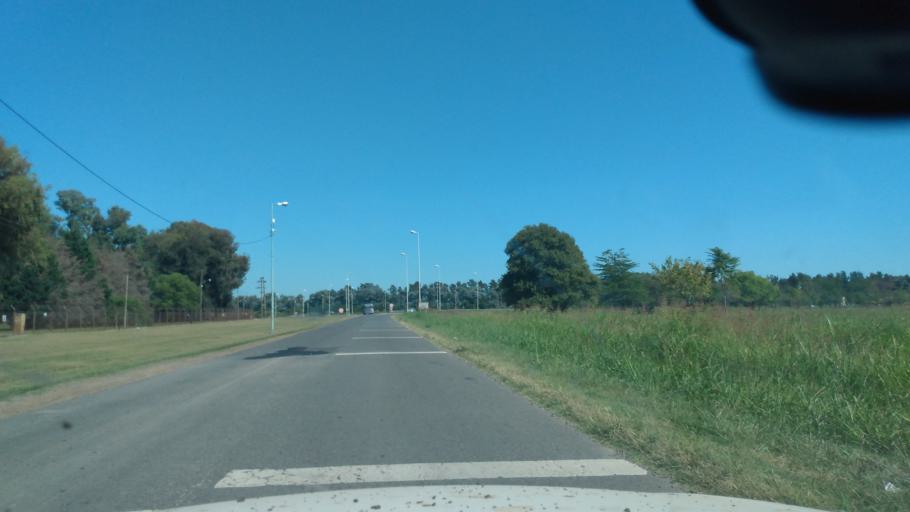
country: AR
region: Buenos Aires
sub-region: Partido de Lujan
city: Lujan
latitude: -34.5091
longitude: -59.0901
